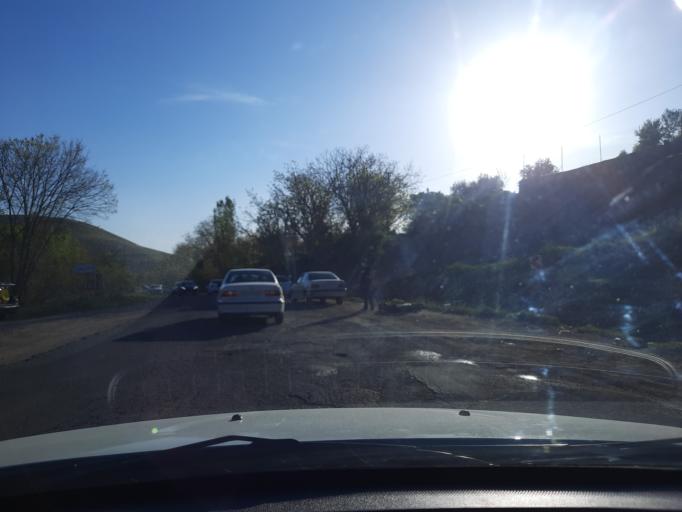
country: IR
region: Qazvin
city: Qazvin
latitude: 36.3446
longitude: 50.1770
